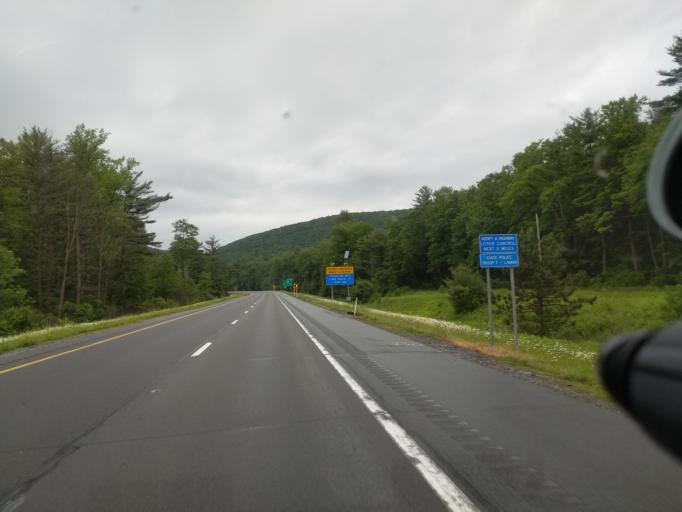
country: US
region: Pennsylvania
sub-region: Union County
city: Mifflinburg
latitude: 41.0468
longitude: -77.1440
